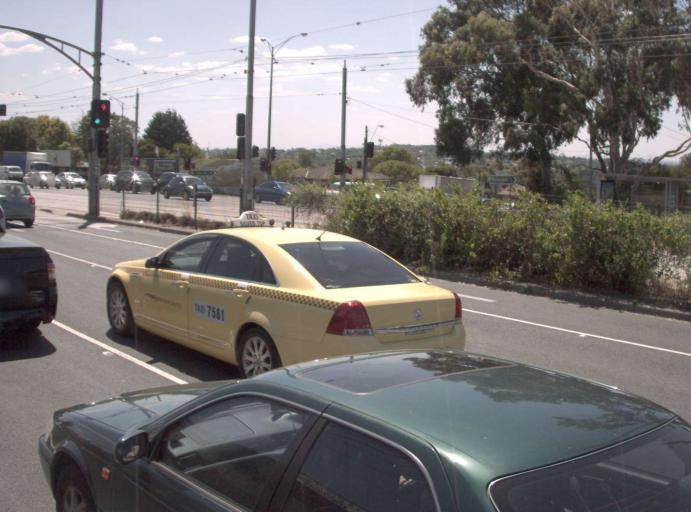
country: AU
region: Victoria
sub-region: Whitehorse
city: Burwood
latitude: -37.8522
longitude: 145.1330
